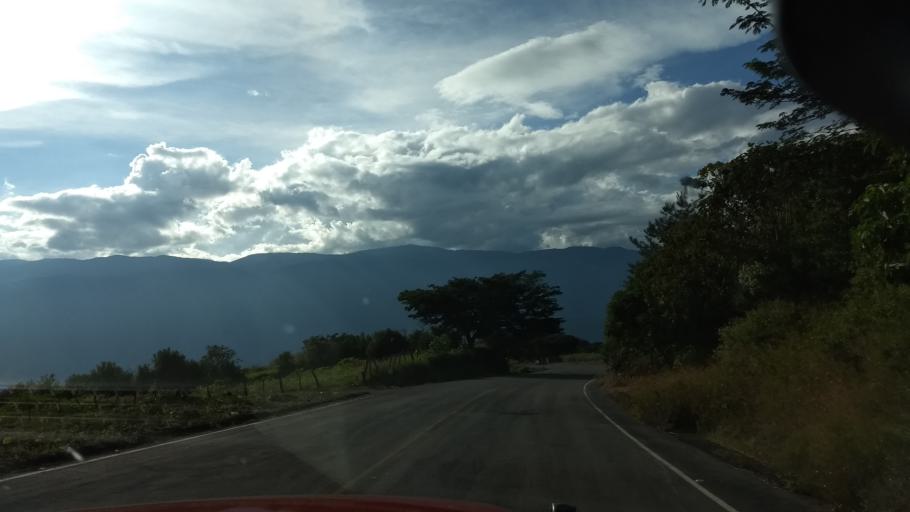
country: MX
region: Colima
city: Suchitlan
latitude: 19.4647
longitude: -103.7759
